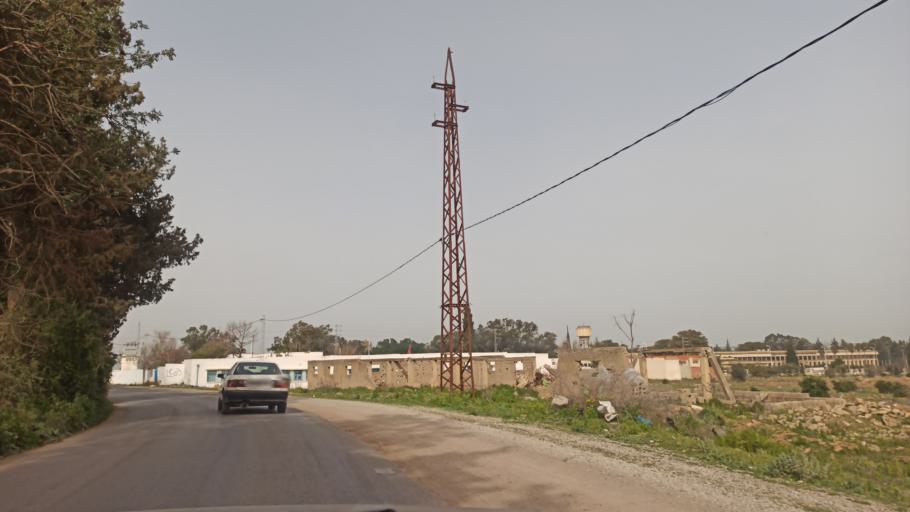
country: TN
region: Zaghwan
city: Zaghouan
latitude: 36.4230
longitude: 10.0949
